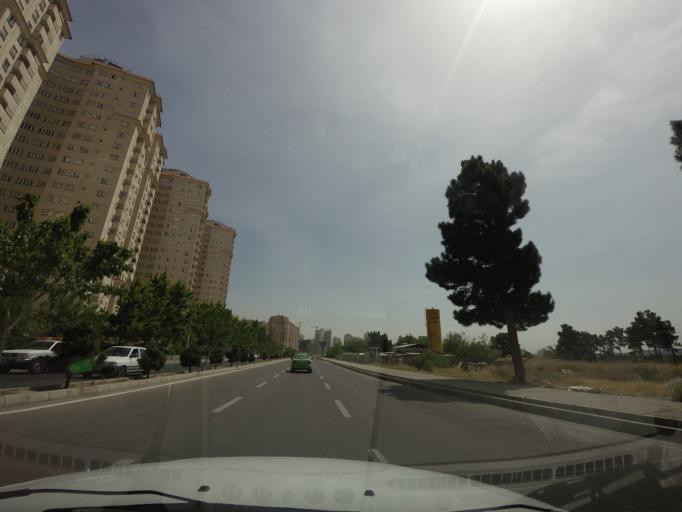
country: IR
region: Tehran
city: Shahr-e Qods
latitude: 35.7529
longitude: 51.1992
